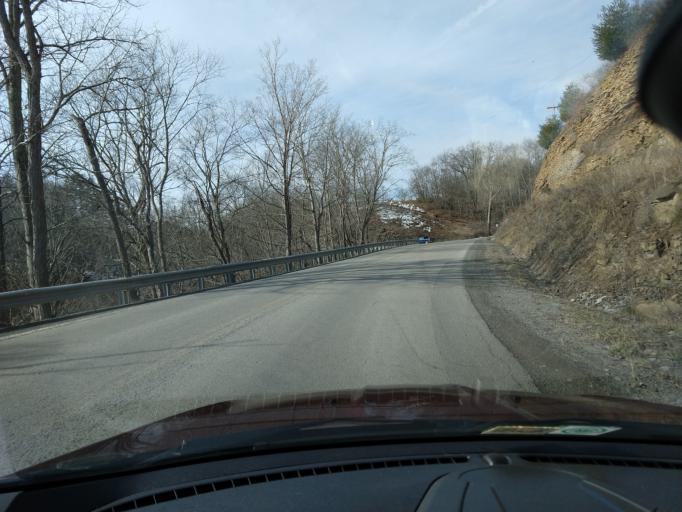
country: US
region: West Virginia
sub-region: Pocahontas County
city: Marlinton
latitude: 38.2115
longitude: -80.1033
